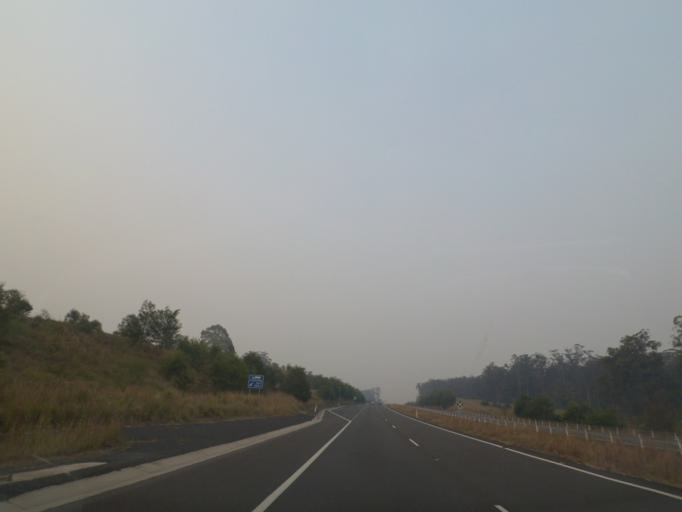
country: AU
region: New South Wales
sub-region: Nambucca Shire
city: Macksville
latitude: -30.7782
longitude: 152.8939
